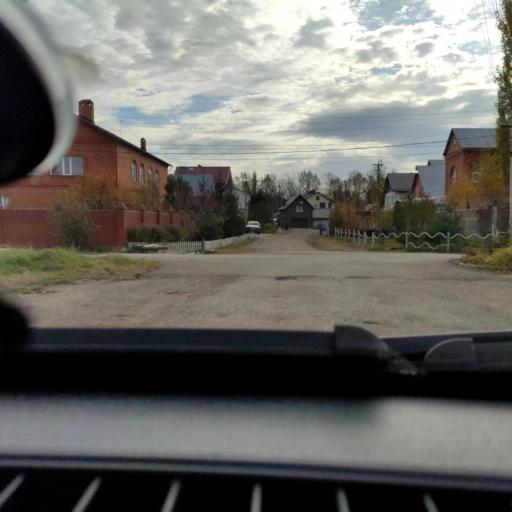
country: RU
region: Bashkortostan
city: Ufa
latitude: 54.7925
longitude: 55.9516
